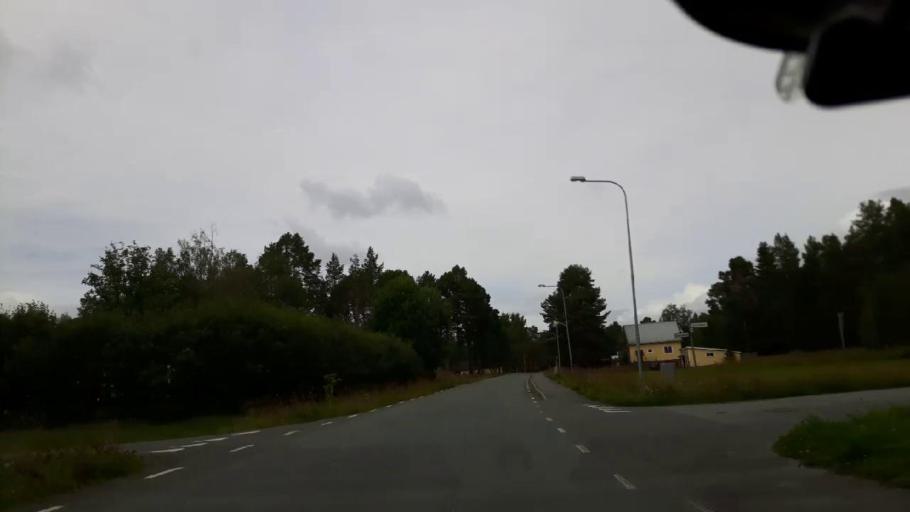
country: SE
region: Jaemtland
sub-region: Krokoms Kommun
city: Valla
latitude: 63.4587
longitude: 14.0622
